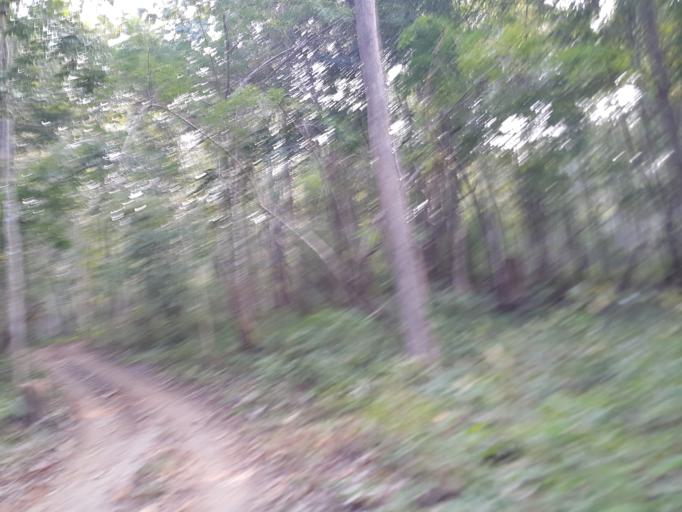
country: TH
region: Lamphun
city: Li
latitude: 17.6211
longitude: 98.9075
